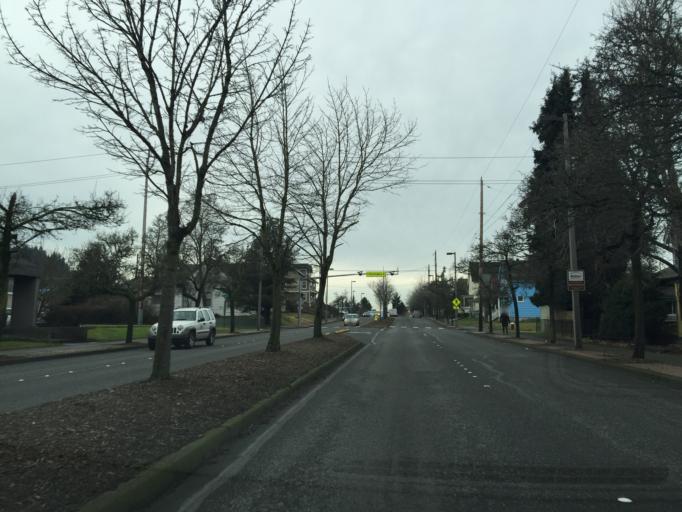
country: US
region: Washington
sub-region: Whatcom County
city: Bellingham
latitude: 48.7451
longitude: -122.4682
